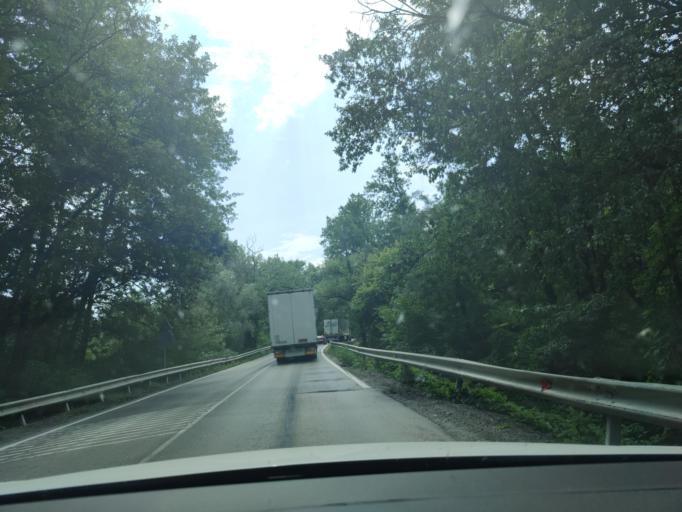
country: BG
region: Vidin
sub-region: Obshtina Dimovo
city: Dimovo
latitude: 43.6772
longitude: 22.7692
